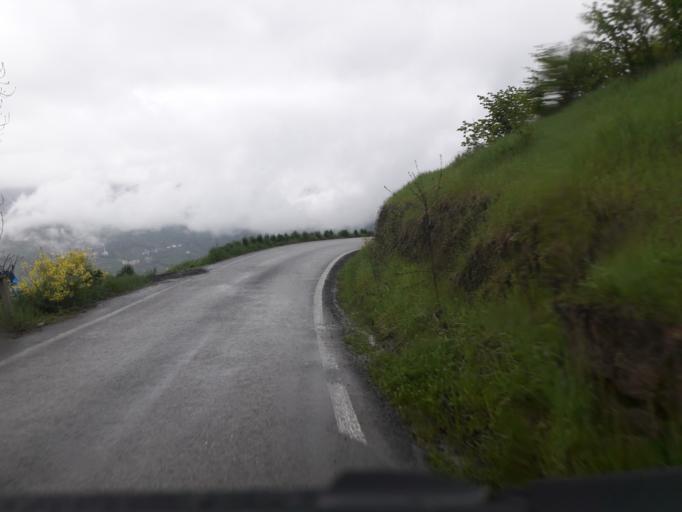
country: TR
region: Trabzon
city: Duzkoy
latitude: 40.9291
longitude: 39.4777
